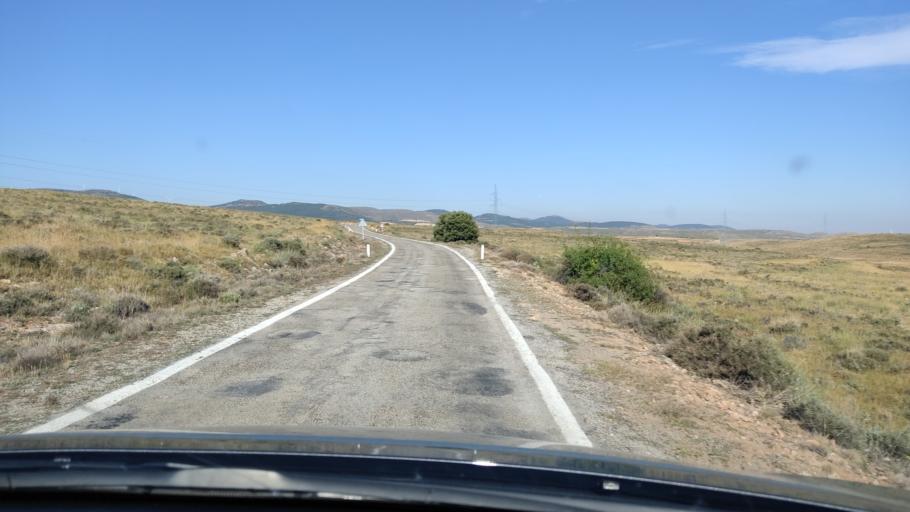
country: ES
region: Aragon
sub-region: Provincia de Teruel
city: Huesa del Comun
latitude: 41.0202
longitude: -0.9609
